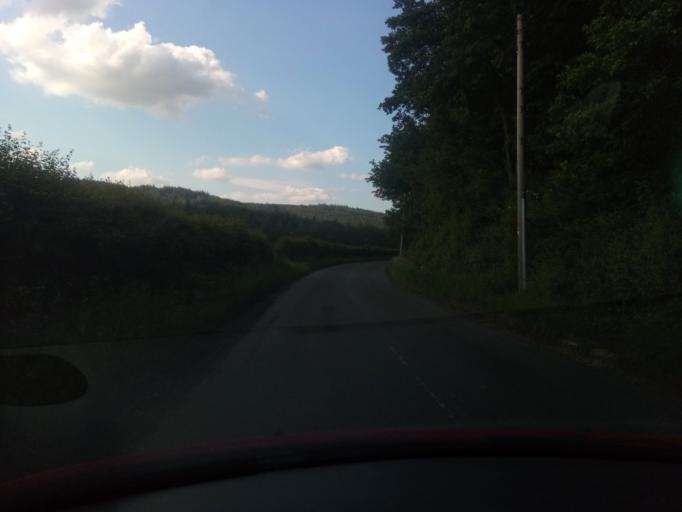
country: GB
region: Scotland
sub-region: The Scottish Borders
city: Selkirk
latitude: 55.5208
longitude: -2.9244
